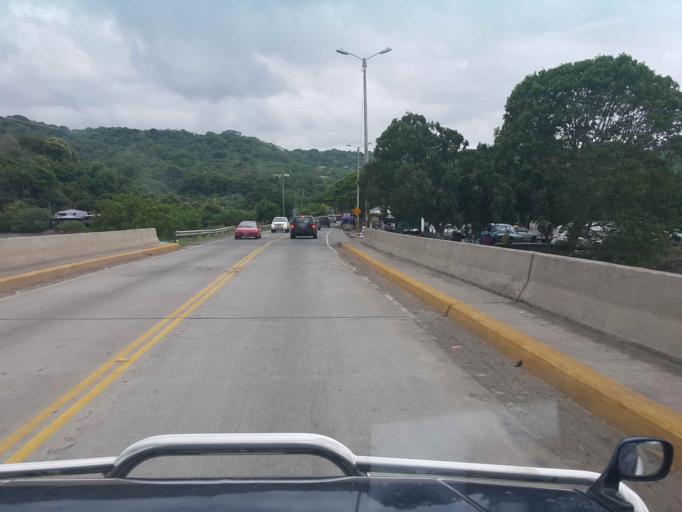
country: CR
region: Puntarenas
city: Esparza
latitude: 9.9222
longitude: -84.7133
